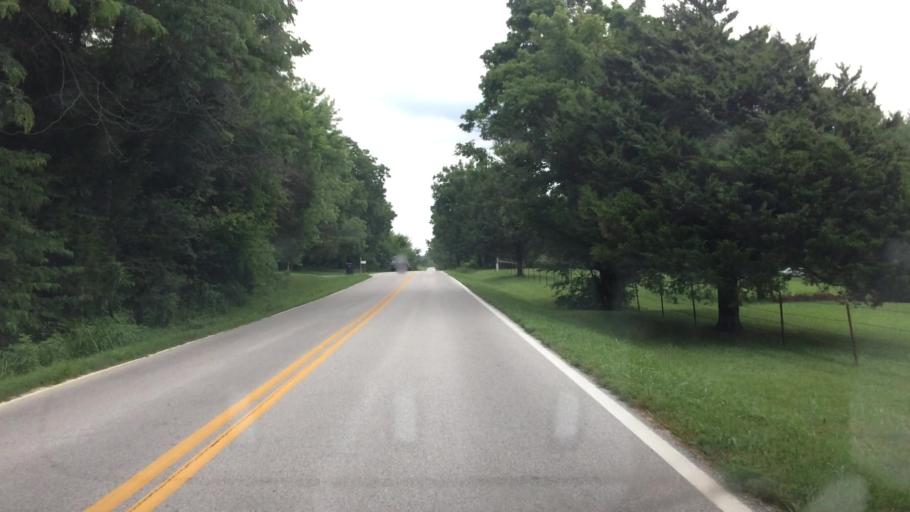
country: US
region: Missouri
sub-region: Greene County
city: Strafford
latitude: 37.3007
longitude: -93.0788
